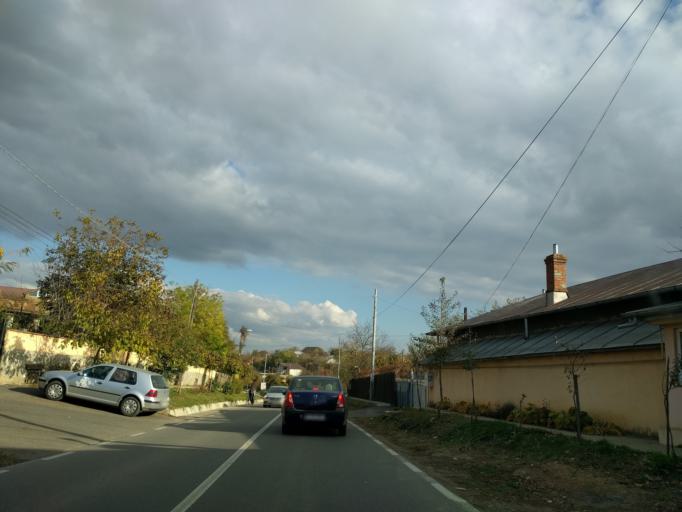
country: RO
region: Ilfov
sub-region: Comuna Branesti
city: Branesti
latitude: 44.4557
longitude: 26.3384
